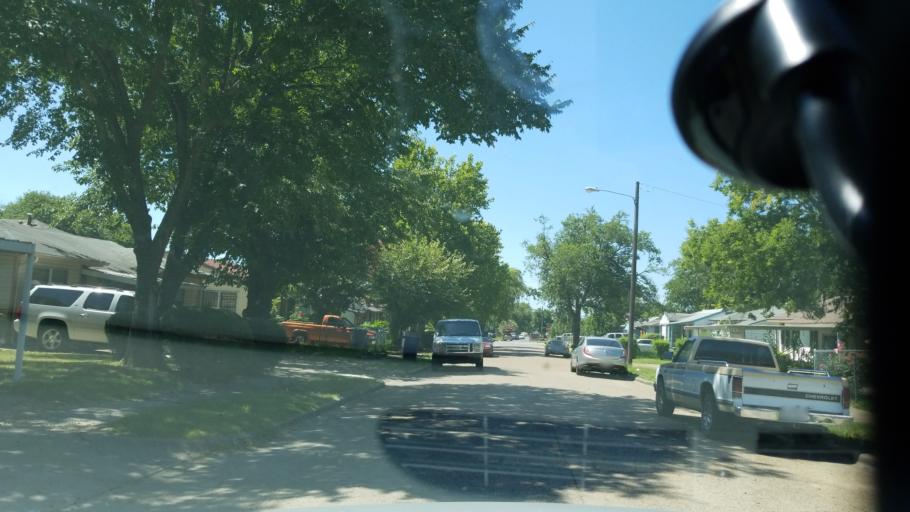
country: US
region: Texas
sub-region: Dallas County
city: Cockrell Hill
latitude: 32.7071
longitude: -96.8171
